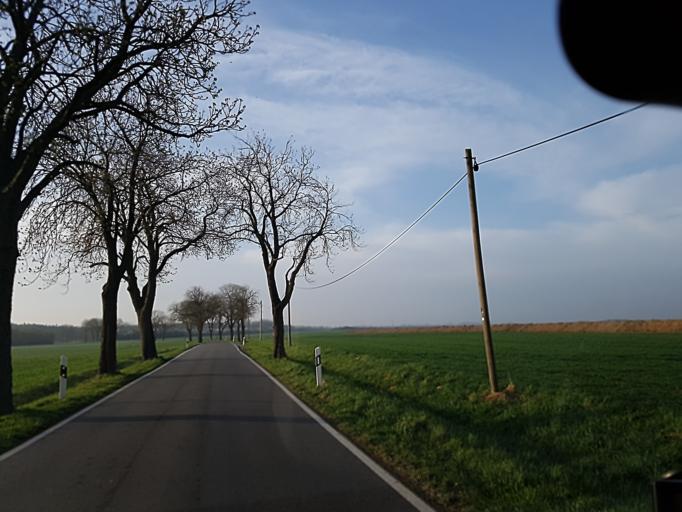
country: DE
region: Brandenburg
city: Muhlberg
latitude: 51.4510
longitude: 13.2657
